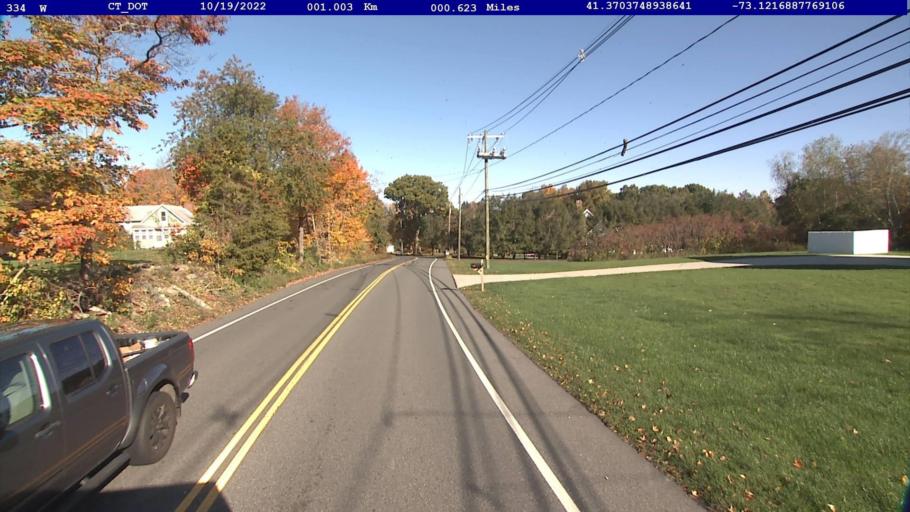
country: US
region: Connecticut
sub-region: New Haven County
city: Ansonia
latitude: 41.3704
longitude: -73.1217
